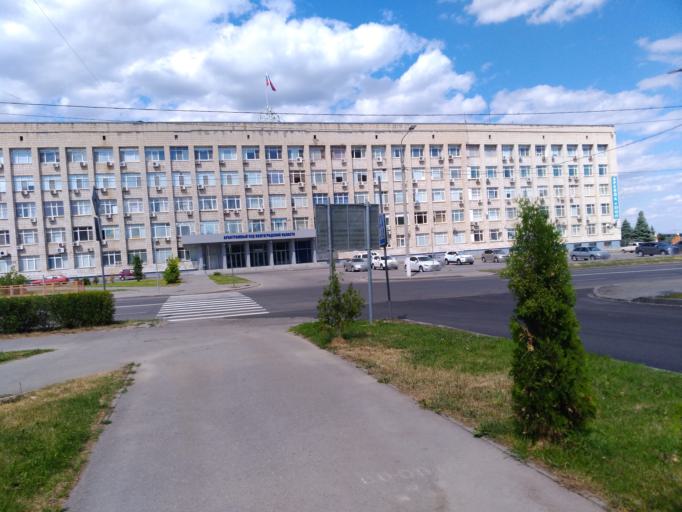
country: RU
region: Volgograd
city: Volgograd
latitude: 48.7213
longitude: 44.5369
